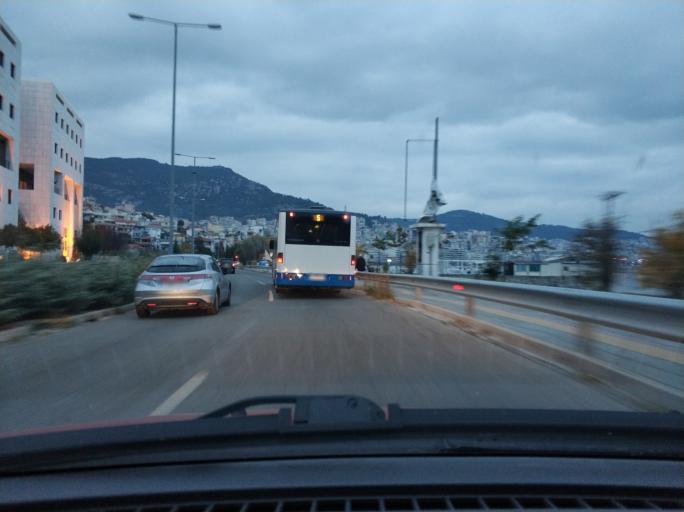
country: GR
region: East Macedonia and Thrace
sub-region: Nomos Kavalas
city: Kavala
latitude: 40.9295
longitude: 24.3915
